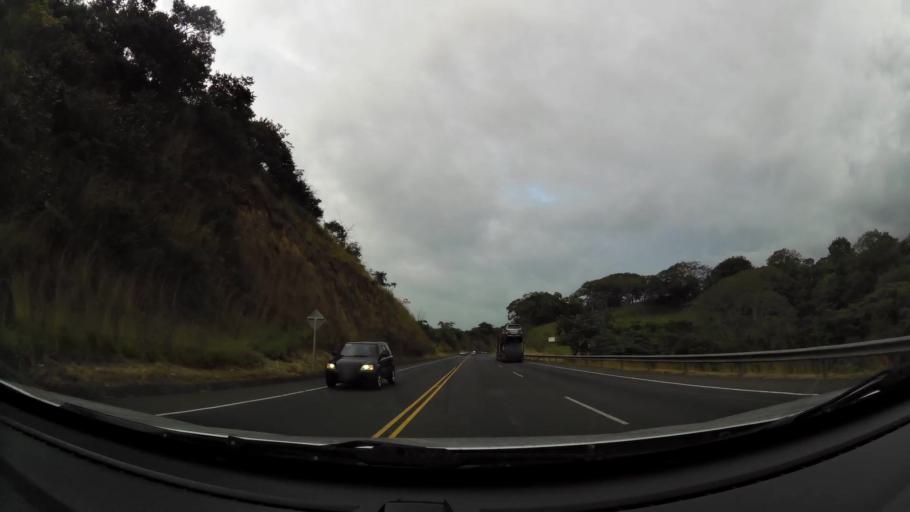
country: CR
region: Alajuela
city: Atenas
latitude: 9.9657
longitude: -84.3380
